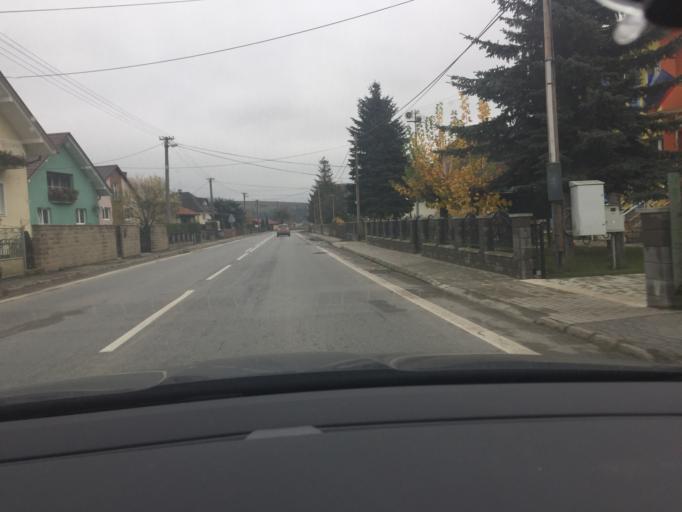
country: SK
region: Presovsky
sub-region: Okres Bardejov
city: Bardejov
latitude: 49.3204
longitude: 21.1699
